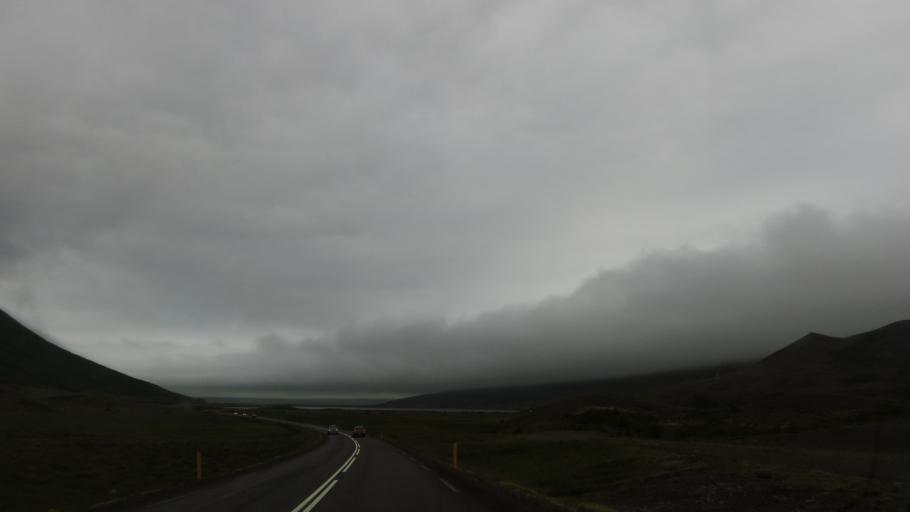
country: IS
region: Northeast
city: Laugar
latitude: 65.7126
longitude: -17.7164
